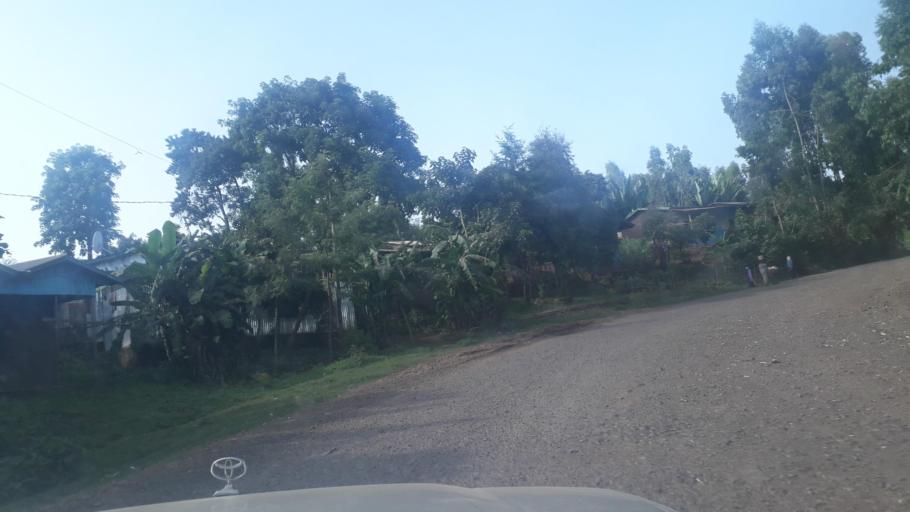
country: ET
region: Oromiya
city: Jima
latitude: 7.4255
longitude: 36.8718
